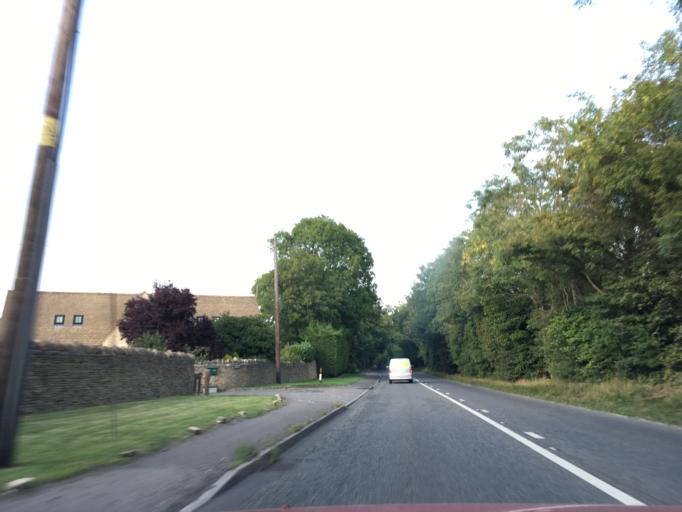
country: GB
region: England
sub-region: Gloucestershire
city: Bourton on the Water
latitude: 51.8819
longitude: -1.7757
